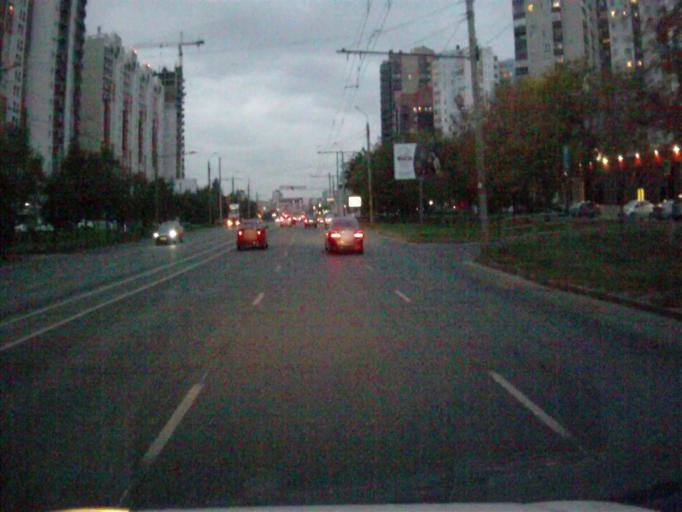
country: RU
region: Chelyabinsk
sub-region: Gorod Chelyabinsk
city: Chelyabinsk
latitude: 55.1754
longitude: 61.3086
